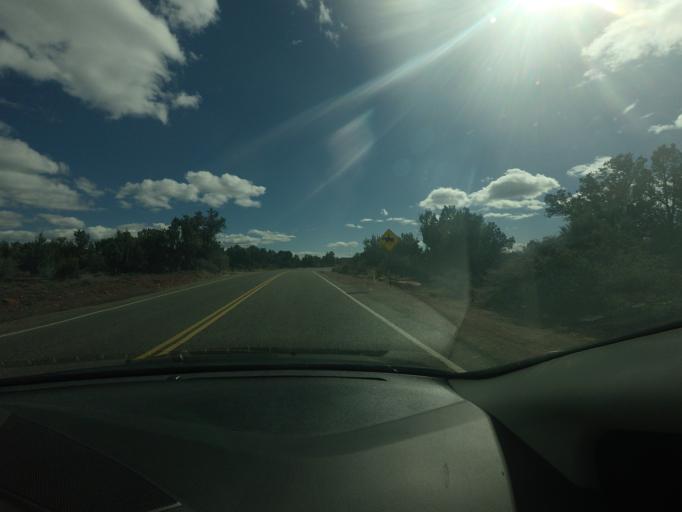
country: US
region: Arizona
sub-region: Yavapai County
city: West Sedona
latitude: 34.8763
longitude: -111.8211
